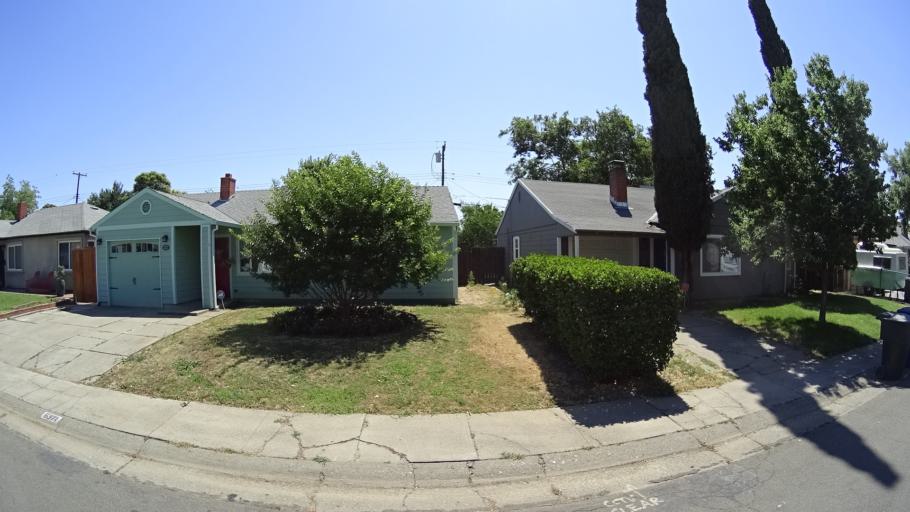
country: US
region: California
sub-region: Sacramento County
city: Florin
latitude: 38.5270
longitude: -121.4160
